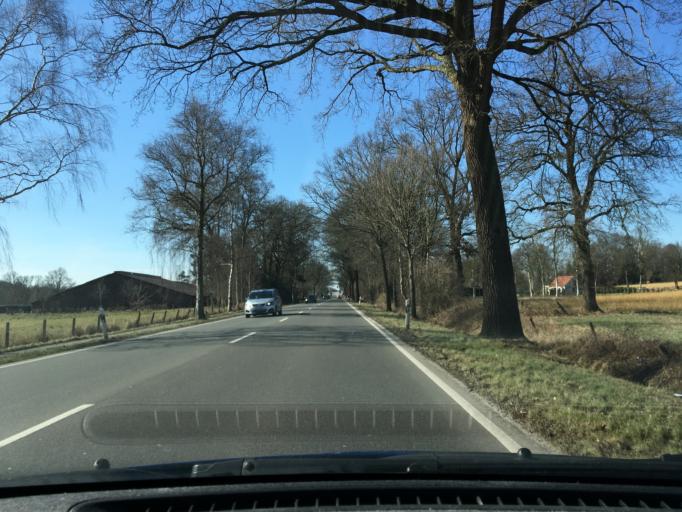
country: DE
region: Lower Saxony
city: Sottrum
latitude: 53.1108
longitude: 9.2118
